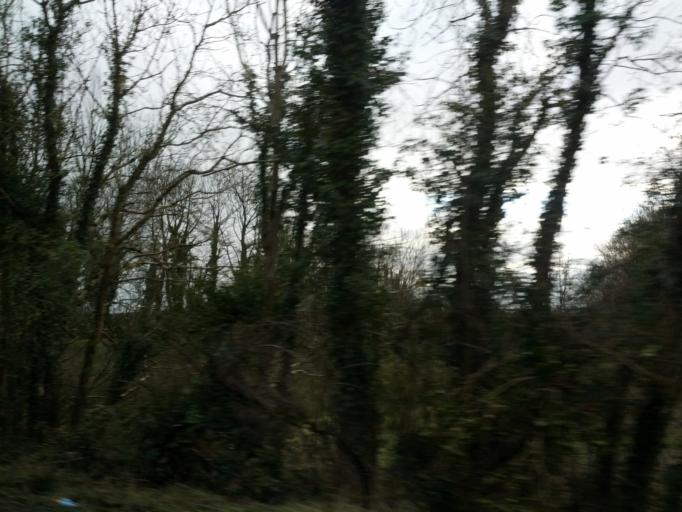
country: IE
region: Connaught
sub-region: County Galway
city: Athenry
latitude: 53.3992
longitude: -8.6269
